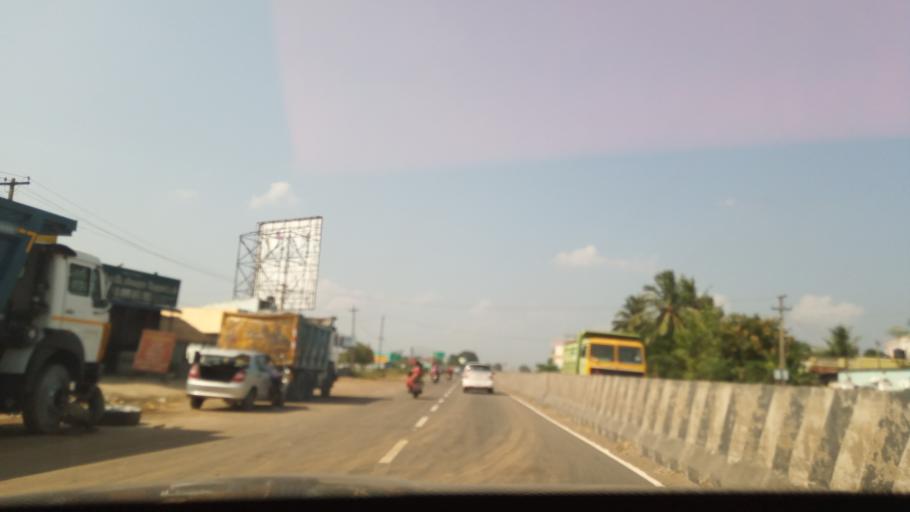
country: IN
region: Tamil Nadu
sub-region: Kancheepuram
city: Madambakkam
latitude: 12.8734
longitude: 79.9897
